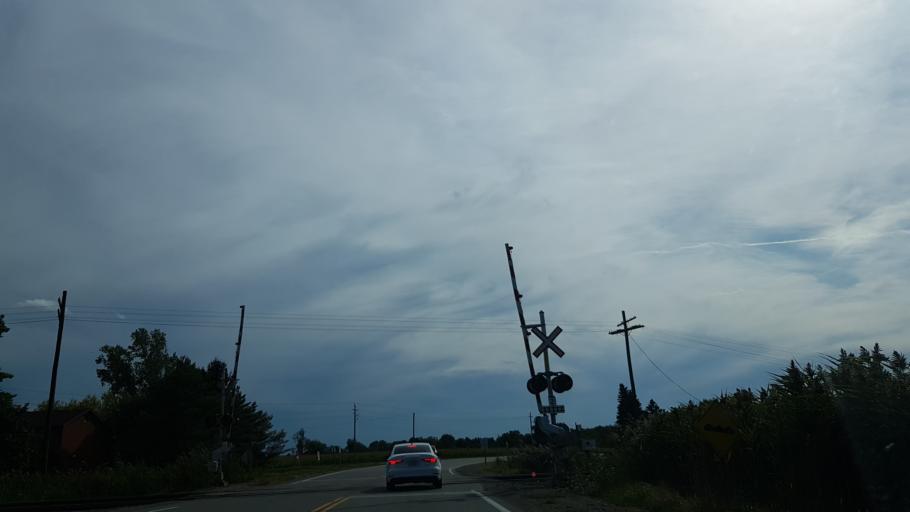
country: CA
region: Ontario
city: Delaware
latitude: 42.9799
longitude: -81.3860
